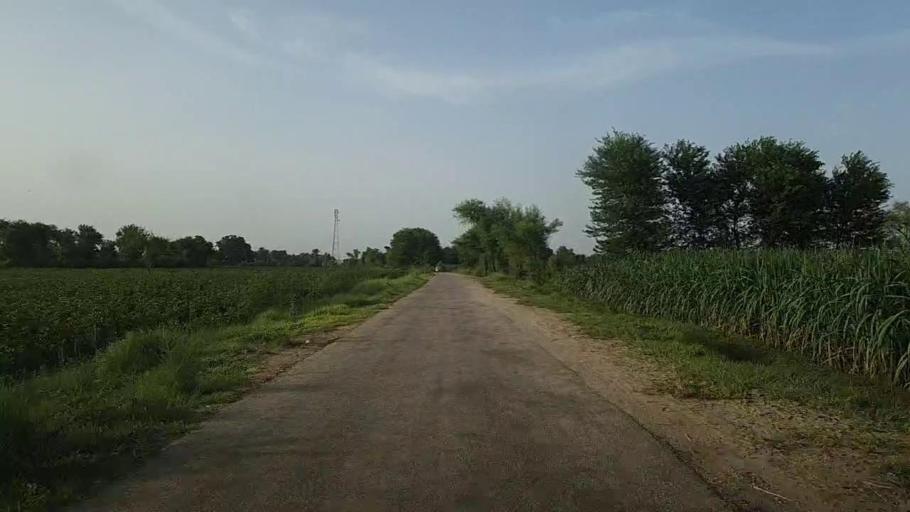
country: PK
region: Sindh
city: Bhiria
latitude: 26.9056
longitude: 68.2635
